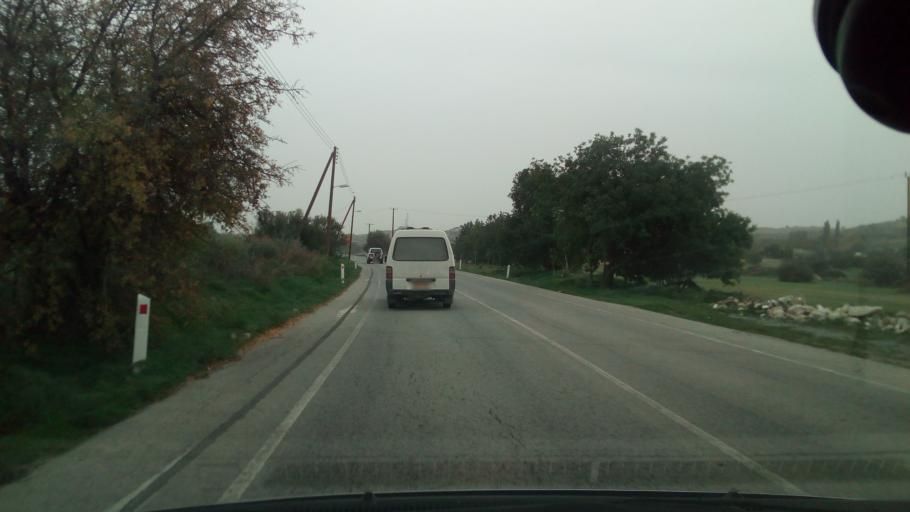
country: CY
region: Larnaka
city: Kofinou
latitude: 34.7928
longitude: 33.3427
